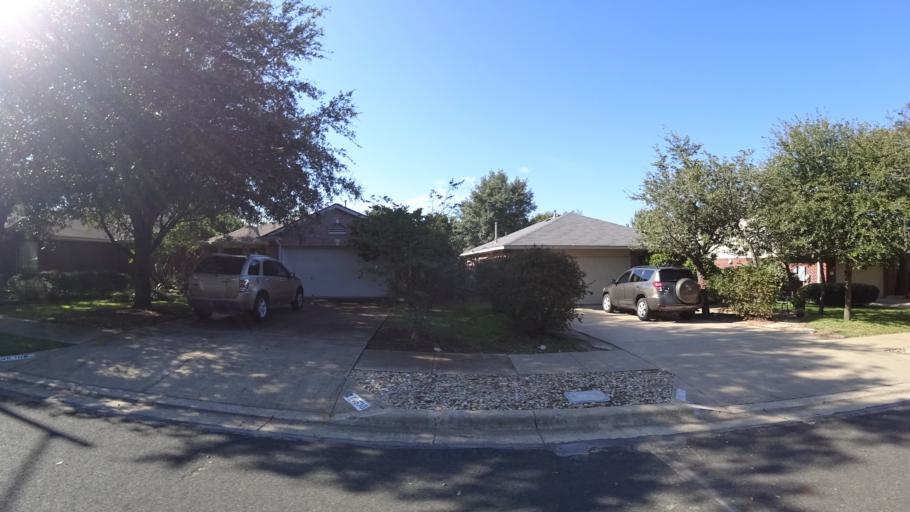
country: US
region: Texas
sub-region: Travis County
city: Shady Hollow
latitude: 30.2023
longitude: -97.8536
